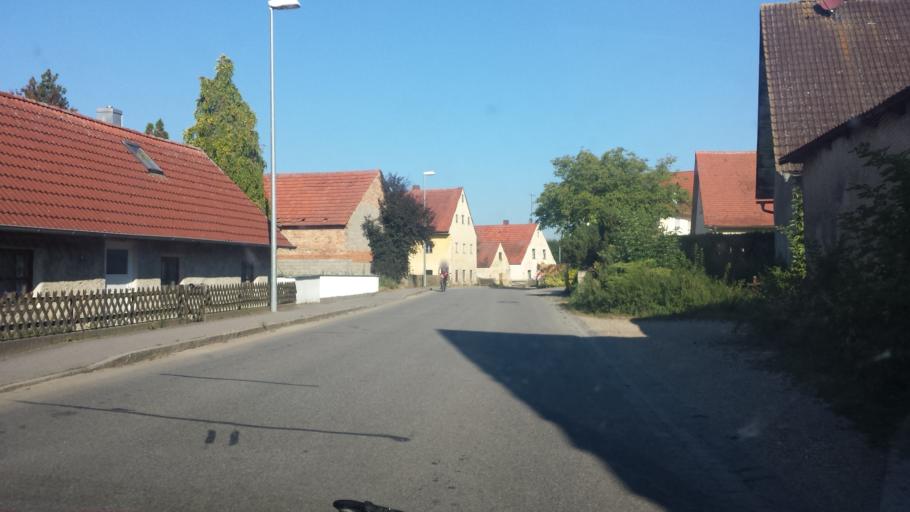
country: DE
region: Bavaria
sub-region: Lower Bavaria
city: Neustadt an der Donau
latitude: 48.8318
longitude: 11.7730
